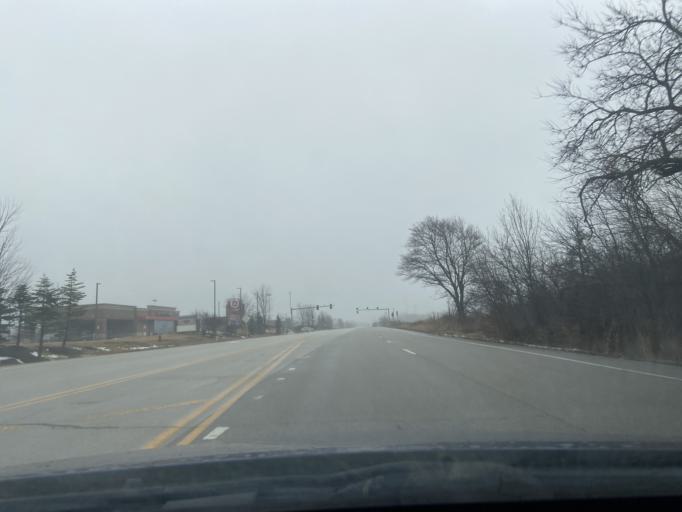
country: US
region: Illinois
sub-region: Lake County
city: Mundelein
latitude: 42.2848
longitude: -88.0493
